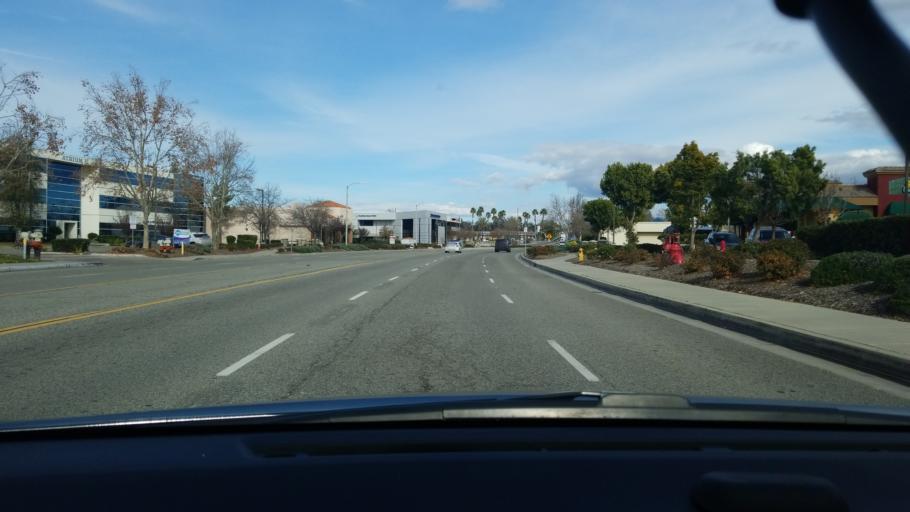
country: US
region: California
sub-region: Riverside County
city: Temecula
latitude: 33.5184
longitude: -117.1680
